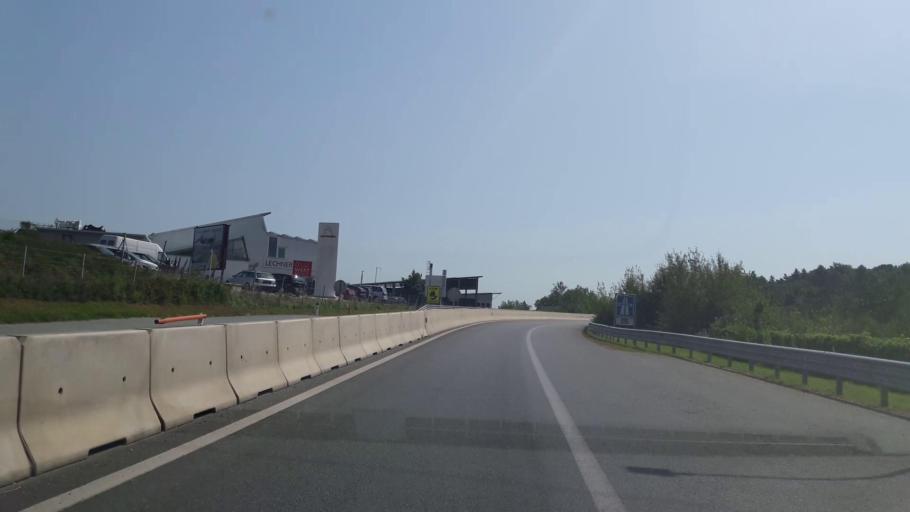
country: AT
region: Styria
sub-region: Politischer Bezirk Hartberg-Fuerstenfeld
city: Sankt Johann in der Haide
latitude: 47.2792
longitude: 16.0081
